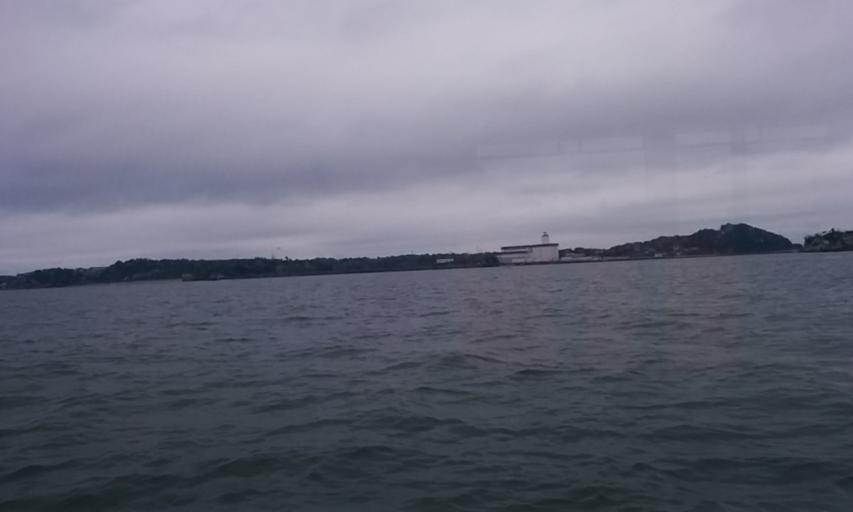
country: JP
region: Miyagi
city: Shiogama
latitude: 38.3245
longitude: 141.0879
